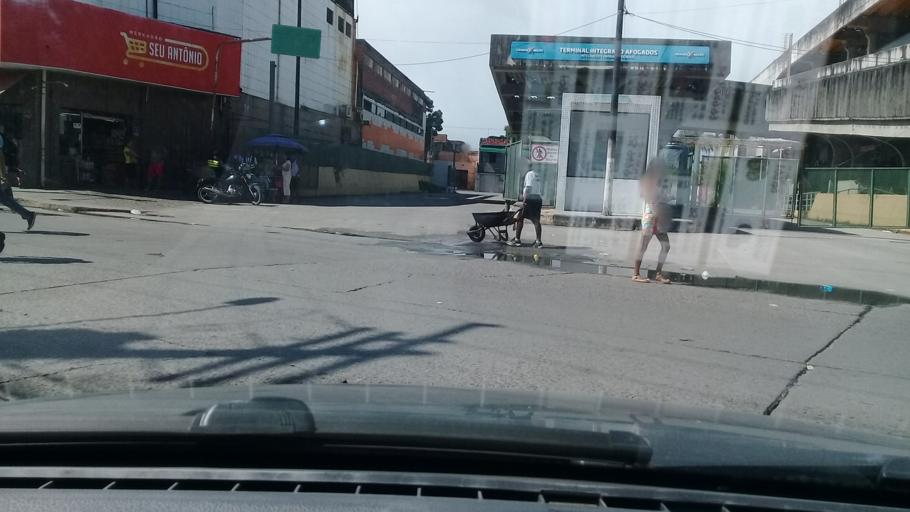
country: BR
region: Pernambuco
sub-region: Recife
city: Recife
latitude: -8.0775
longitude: -34.9071
